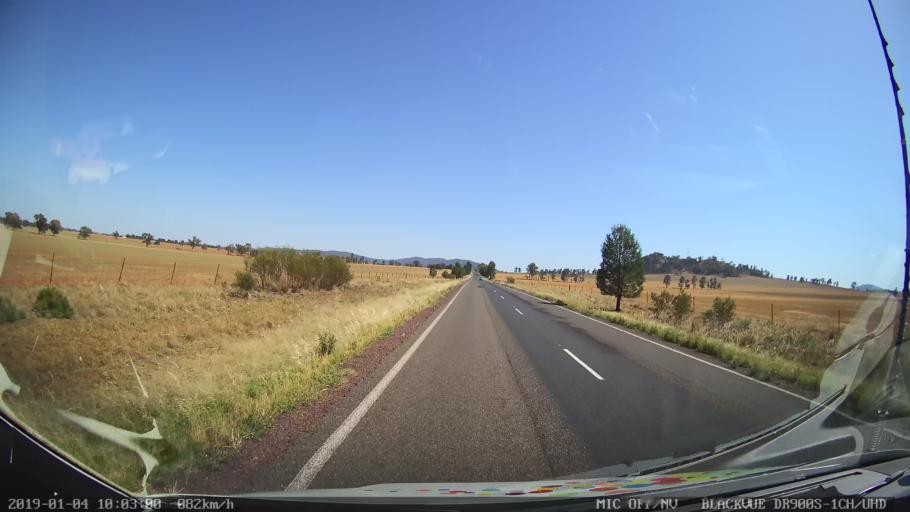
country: AU
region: New South Wales
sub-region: Cabonne
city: Canowindra
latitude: -33.4693
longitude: 148.3648
